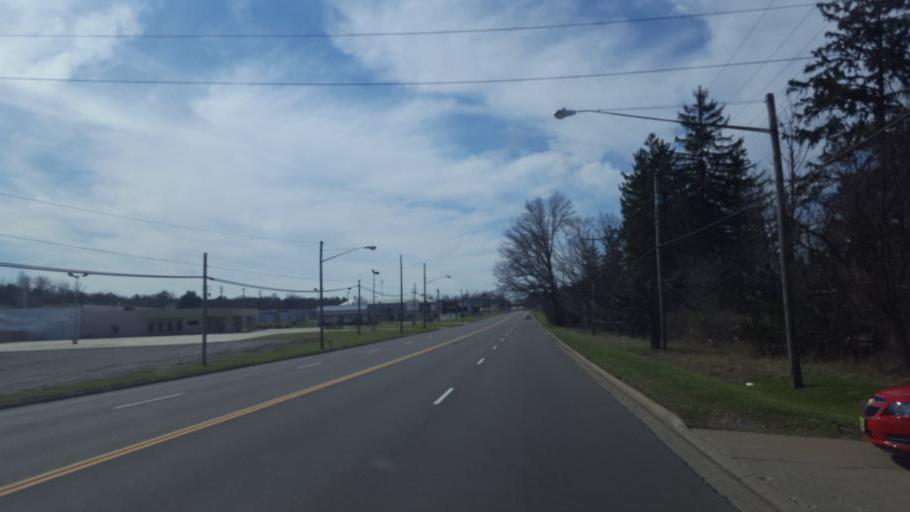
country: US
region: Ohio
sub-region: Richland County
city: Ontario
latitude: 40.7669
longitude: -82.5576
